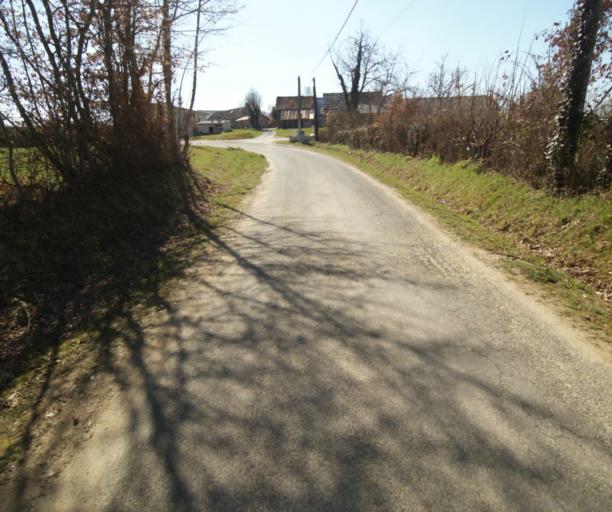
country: FR
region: Limousin
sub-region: Departement de la Correze
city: Saint-Mexant
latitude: 45.3086
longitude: 1.6014
